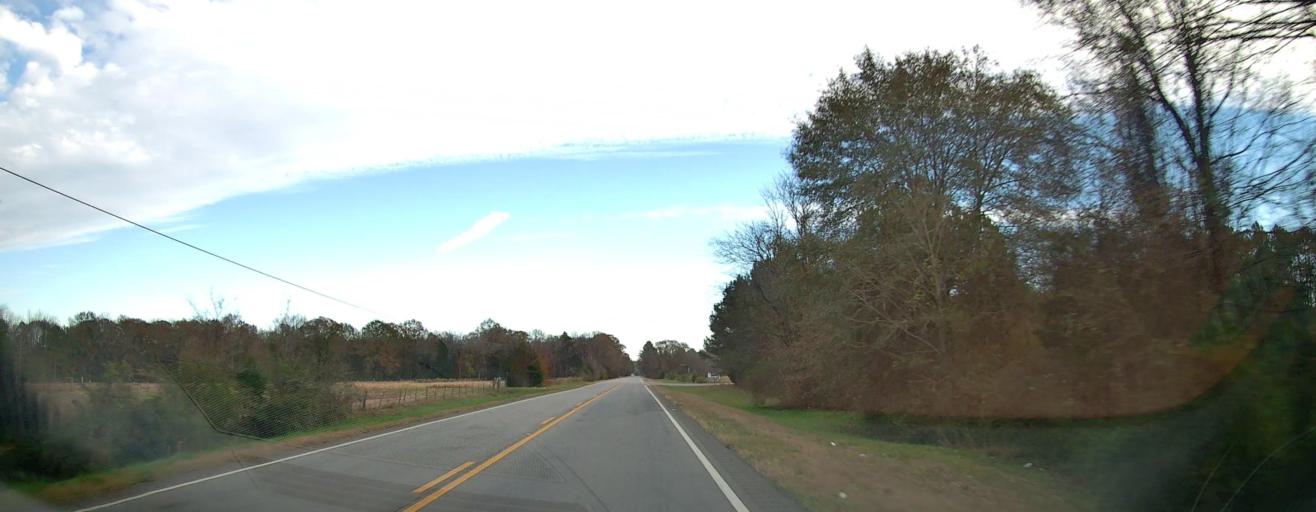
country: US
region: Alabama
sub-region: Marshall County
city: Arab
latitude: 34.3967
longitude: -86.6781
